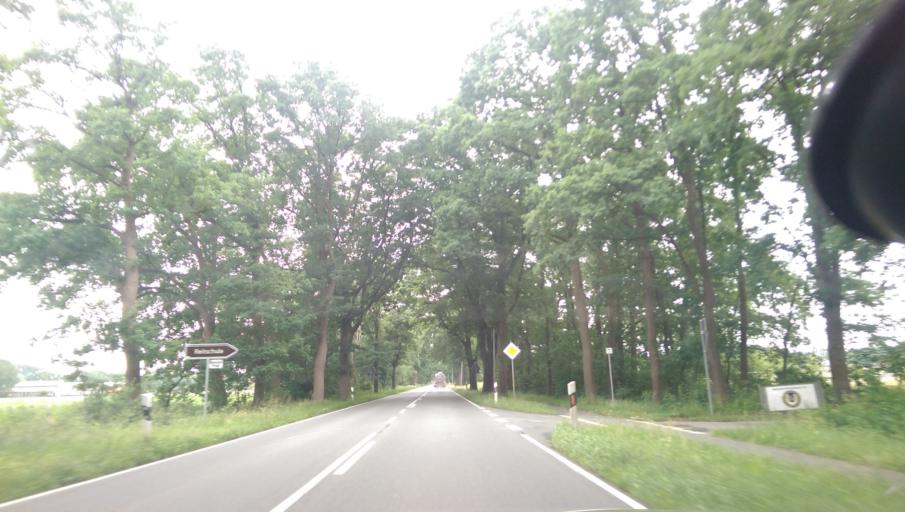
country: DE
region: Lower Saxony
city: Rotenburg
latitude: 53.0920
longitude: 9.4128
